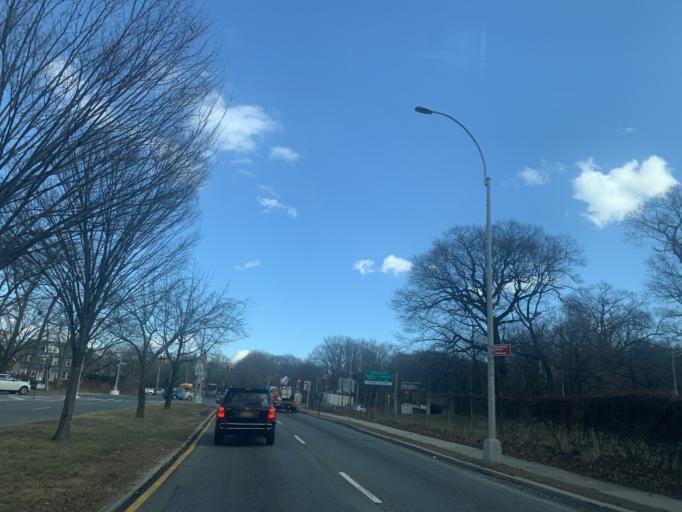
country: US
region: New York
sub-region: Queens County
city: Borough of Queens
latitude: 40.7088
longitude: -73.8440
